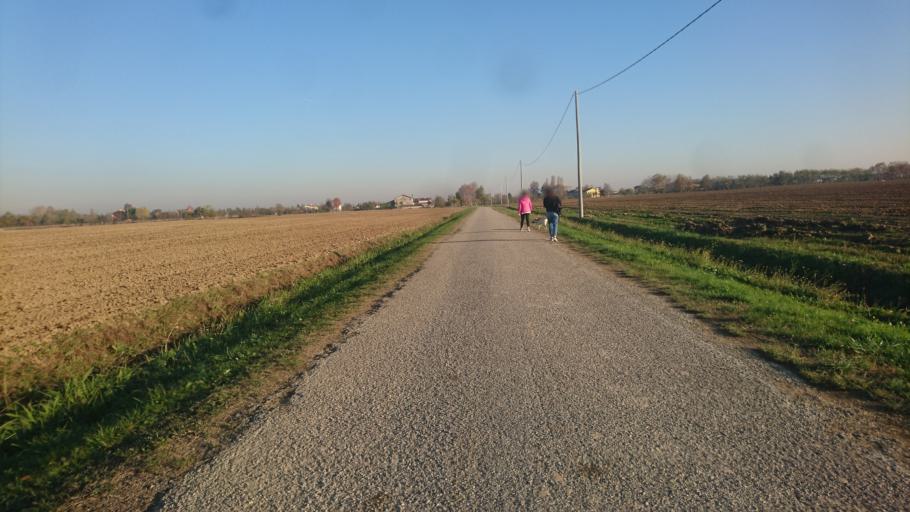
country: IT
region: Veneto
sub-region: Provincia di Padova
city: Bosco
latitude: 45.4464
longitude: 11.8001
